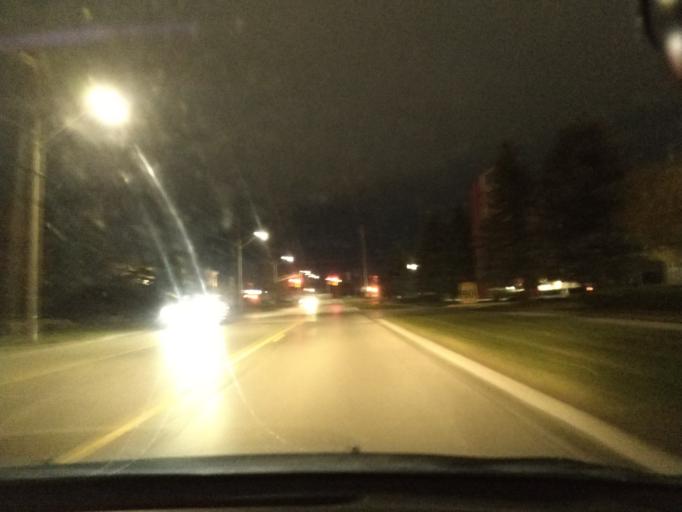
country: CA
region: Ontario
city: Innisfil
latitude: 44.3377
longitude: -79.6895
